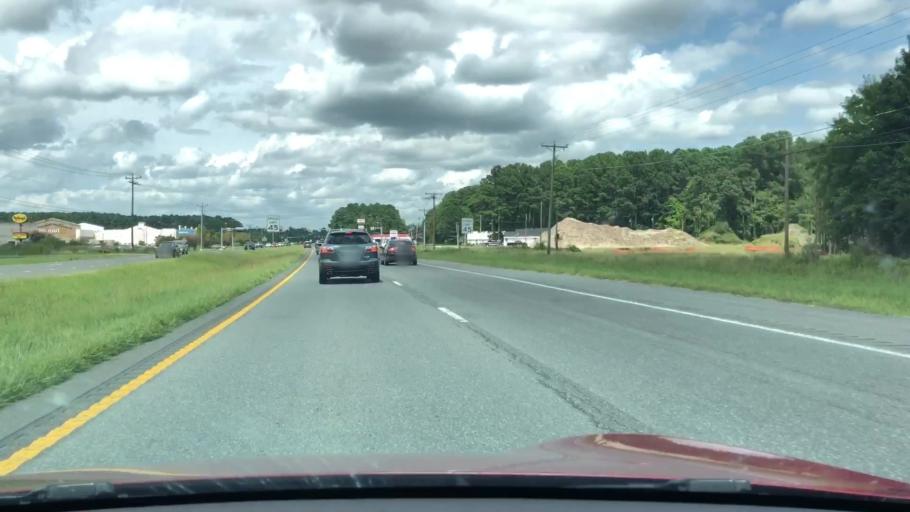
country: US
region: Virginia
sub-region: Accomack County
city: Onancock
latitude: 37.6812
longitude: -75.7227
